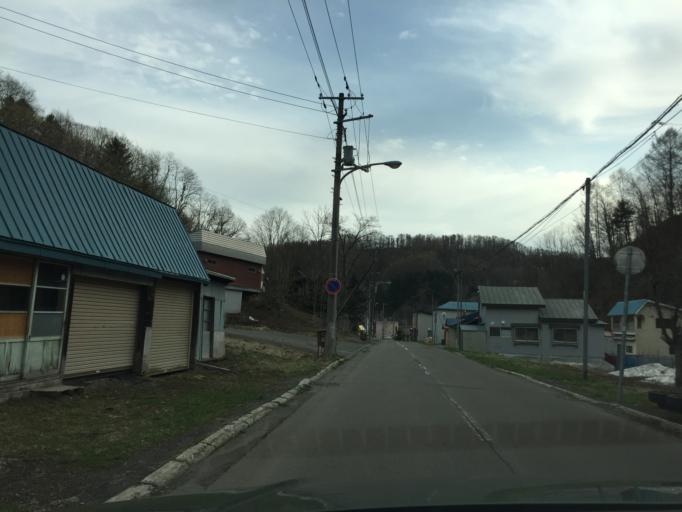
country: JP
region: Hokkaido
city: Utashinai
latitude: 43.5248
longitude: 142.0415
